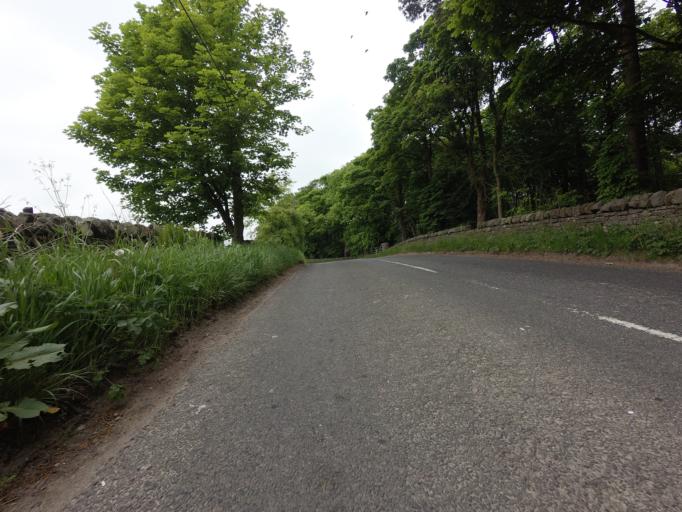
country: GB
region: Scotland
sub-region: Fife
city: Townhill
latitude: 56.1060
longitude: -3.4538
